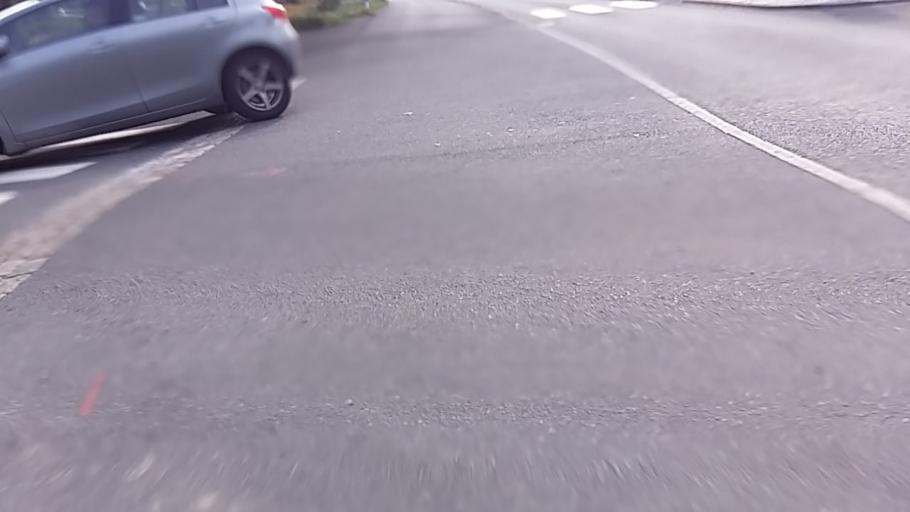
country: SE
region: Joenkoeping
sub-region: Jonkopings Kommun
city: Jonkoping
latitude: 57.7563
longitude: 14.1521
